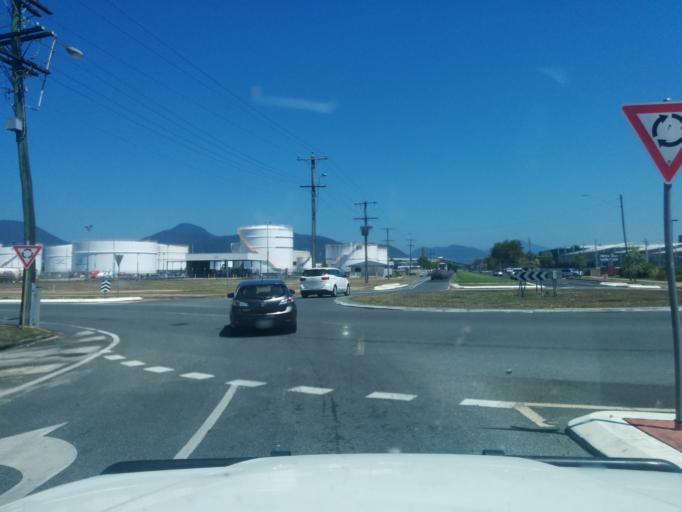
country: AU
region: Queensland
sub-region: Cairns
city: Cairns
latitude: -16.9324
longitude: 145.7736
